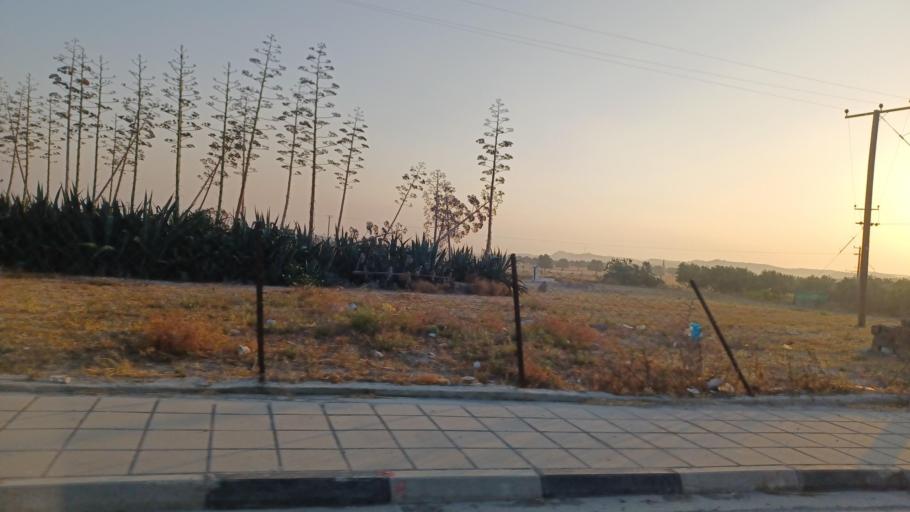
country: CY
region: Larnaka
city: Tersefanou
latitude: 34.8930
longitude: 33.5192
